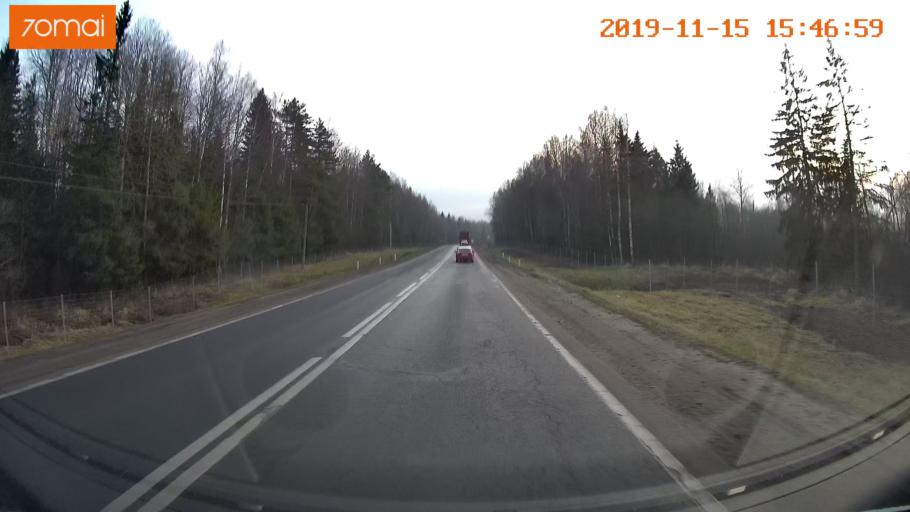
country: RU
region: Jaroslavl
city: Danilov
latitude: 57.9435
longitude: 40.0123
